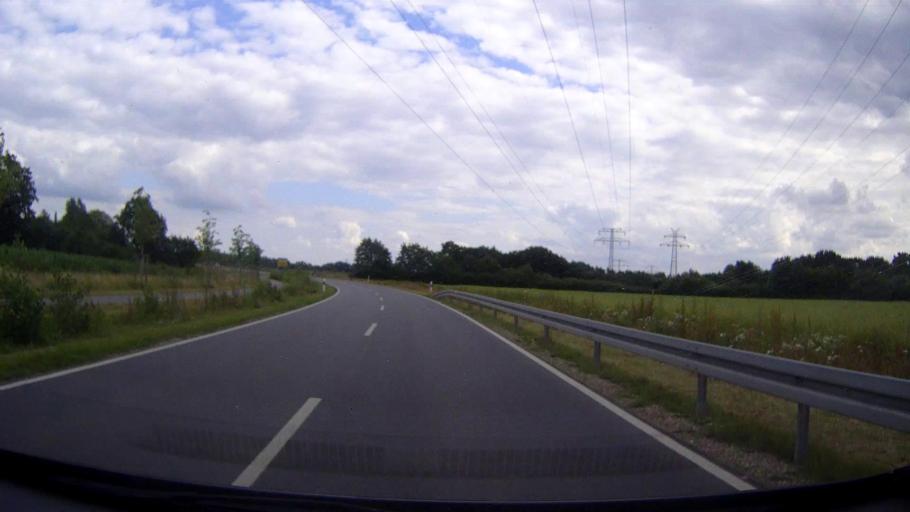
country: DE
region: Schleswig-Holstein
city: Badendorf
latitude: 53.8770
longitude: 10.6025
